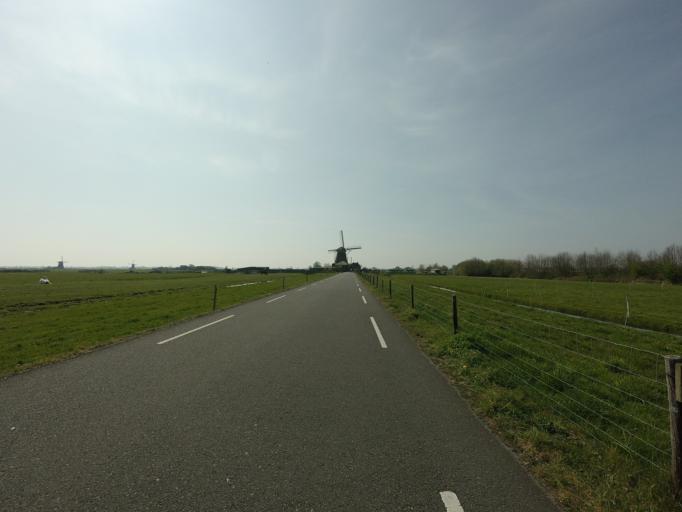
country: NL
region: South Holland
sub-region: Gemeente Nieuwkoop
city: Nieuwkoop
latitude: 52.1367
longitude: 4.7231
